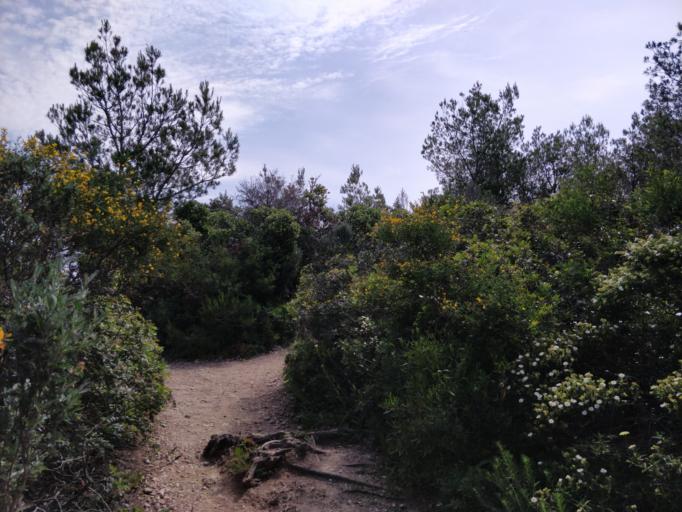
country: FR
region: Provence-Alpes-Cote d'Azur
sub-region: Departement du Var
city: Hyeres
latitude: 43.0346
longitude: 6.1686
